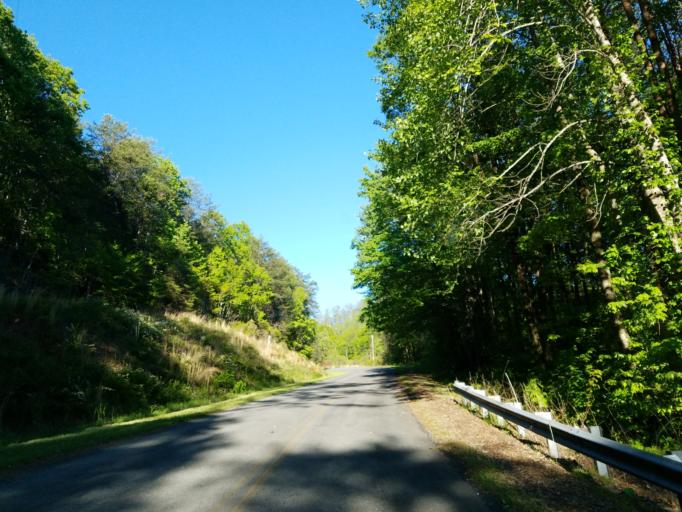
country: US
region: Georgia
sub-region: Fannin County
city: Blue Ridge
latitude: 34.7224
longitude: -84.2869
